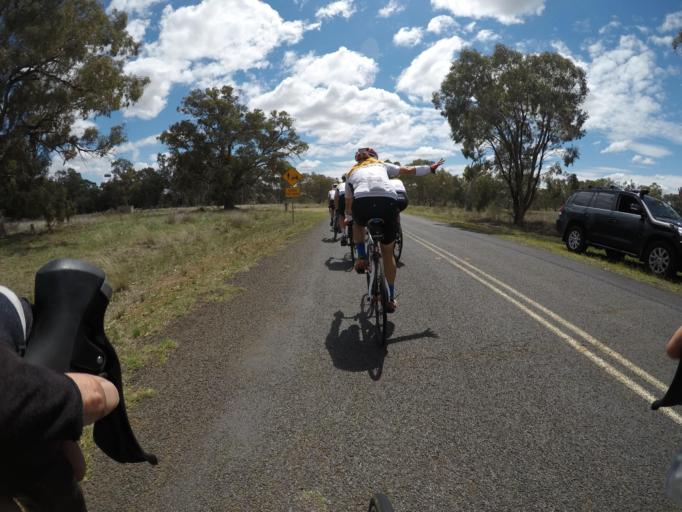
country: AU
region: New South Wales
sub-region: Dubbo Municipality
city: Dubbo
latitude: -32.3904
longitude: 148.5716
